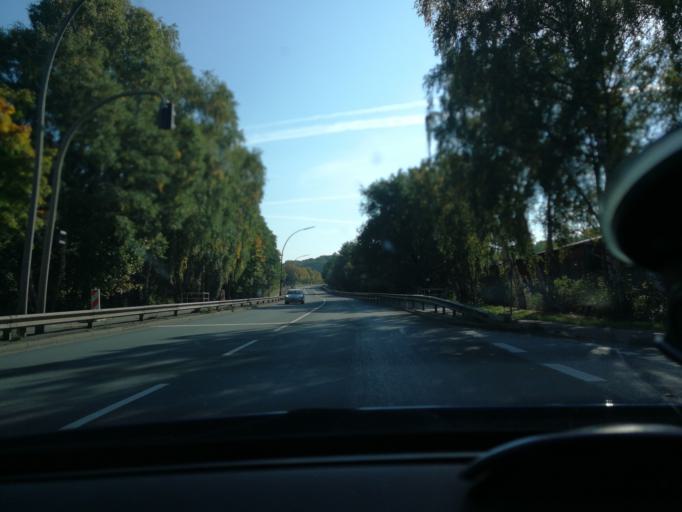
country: DE
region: Hamburg
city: Altona
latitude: 53.4760
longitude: 9.8993
